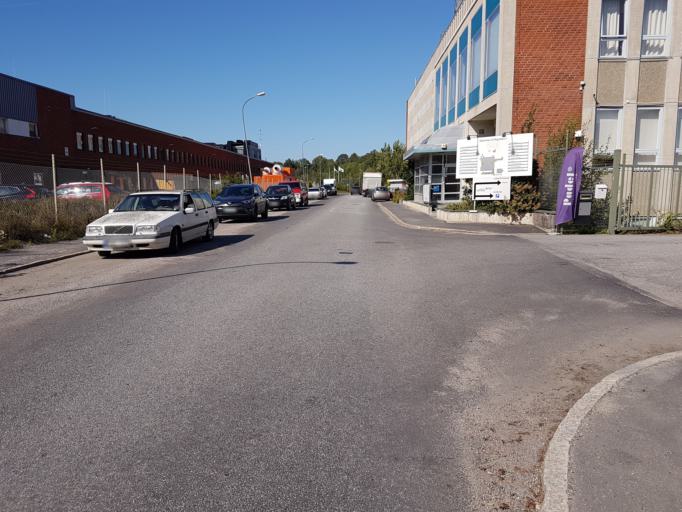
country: SE
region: Stockholm
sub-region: Huddinge Kommun
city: Huddinge
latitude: 59.2217
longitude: 17.9568
